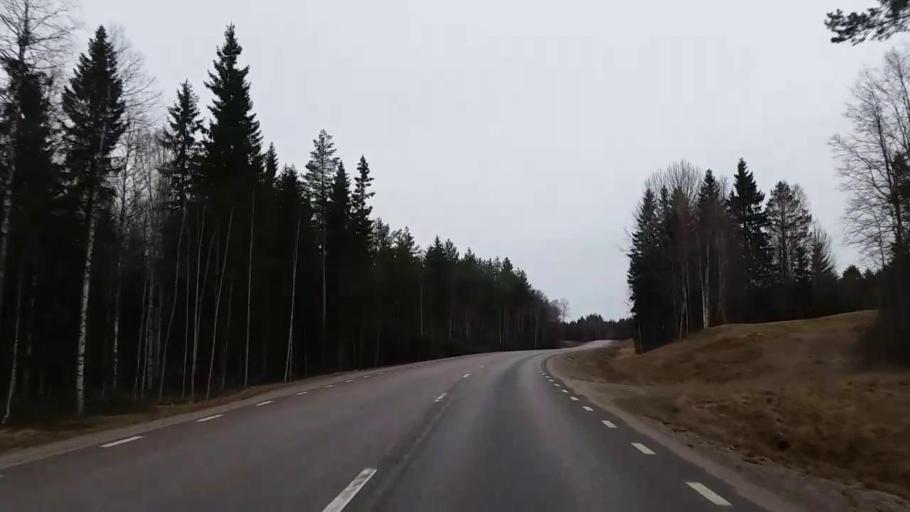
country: SE
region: Gaevleborg
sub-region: Ovanakers Kommun
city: Edsbyn
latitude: 61.1955
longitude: 15.8739
